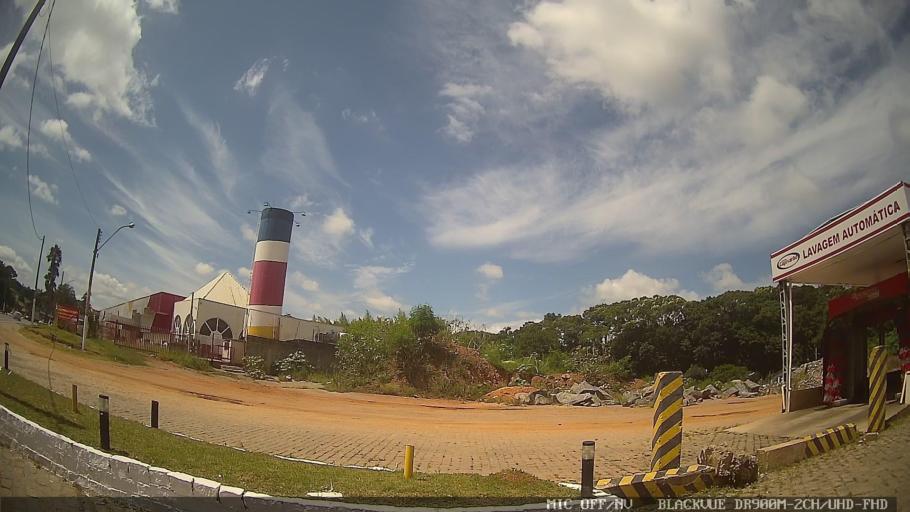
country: BR
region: Sao Paulo
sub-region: Braganca Paulista
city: Braganca Paulista
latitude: -22.9819
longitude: -46.5343
